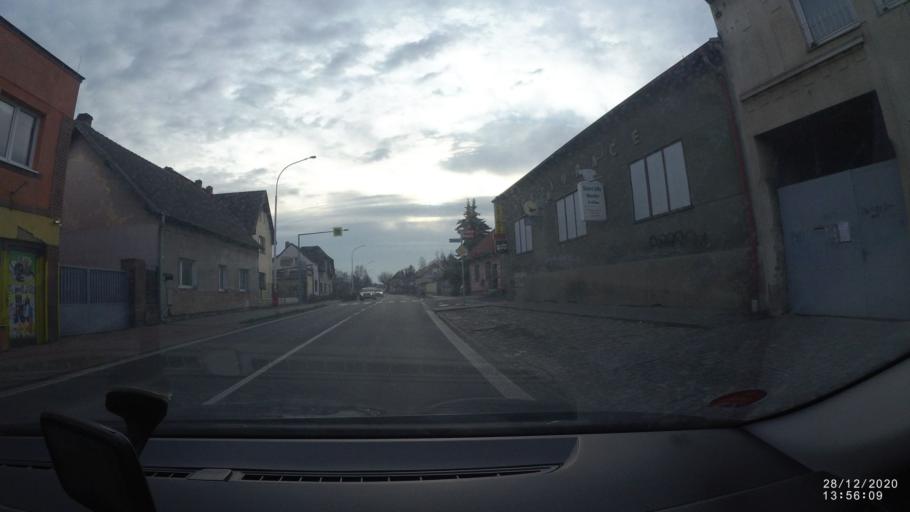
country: CZ
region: Central Bohemia
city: Sestajovice
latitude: 50.1085
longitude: 14.6817
